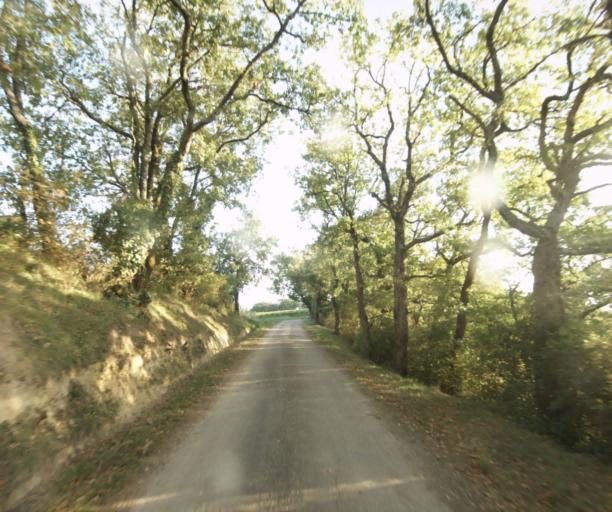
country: FR
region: Midi-Pyrenees
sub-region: Departement du Gers
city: Gondrin
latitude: 43.8769
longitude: 0.2861
